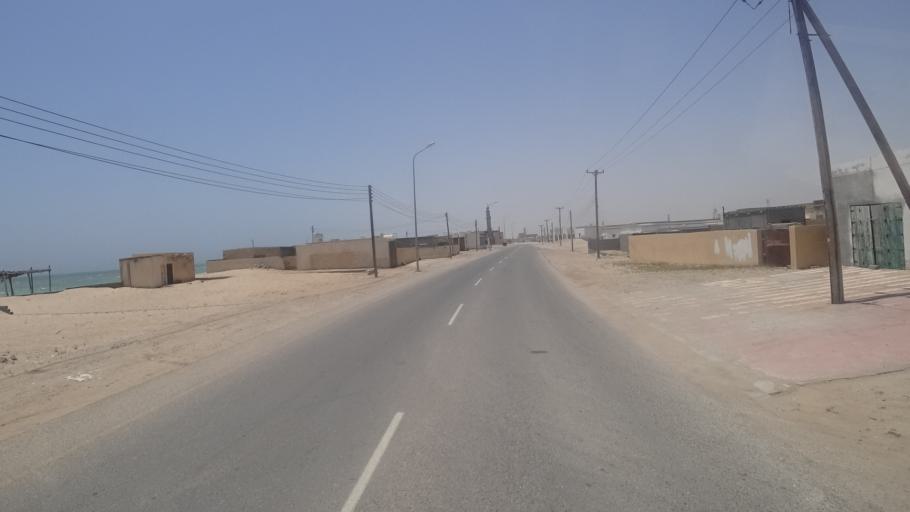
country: OM
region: Ash Sharqiyah
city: Sur
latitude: 22.0873
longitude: 59.6889
